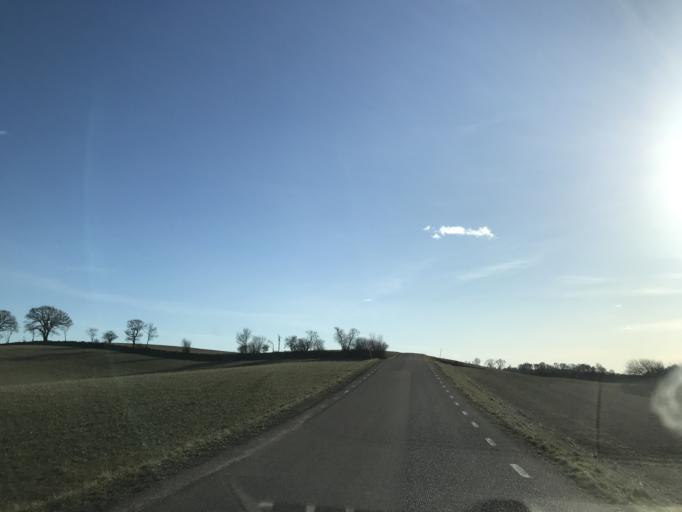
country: SE
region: Skane
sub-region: Ystads Kommun
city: Ystad
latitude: 55.5439
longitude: 13.7895
